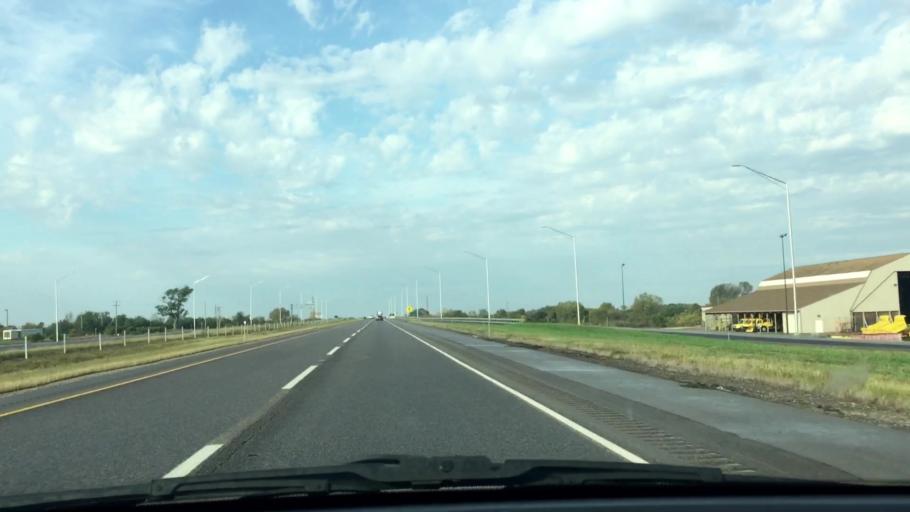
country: US
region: Illinois
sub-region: Lee County
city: Dixon
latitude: 41.8203
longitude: -89.4680
